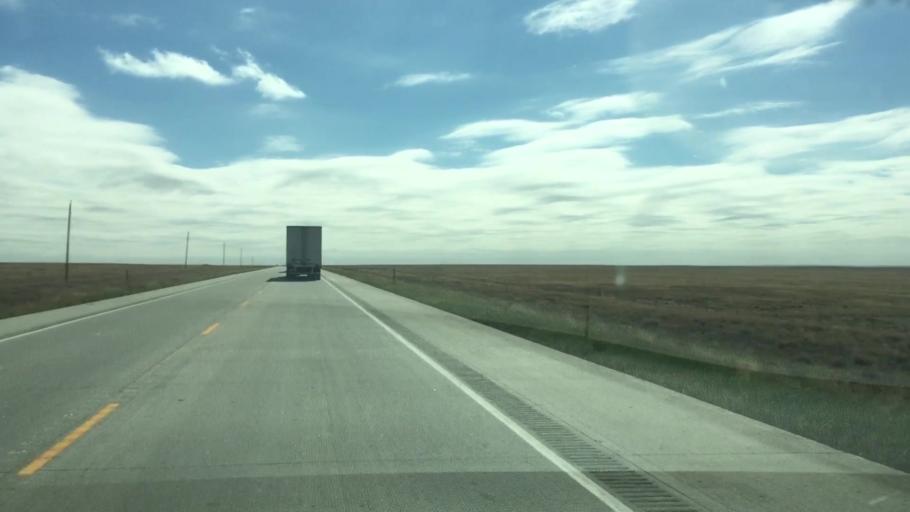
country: US
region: Colorado
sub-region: Lincoln County
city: Hugo
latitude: 39.0205
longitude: -103.3114
